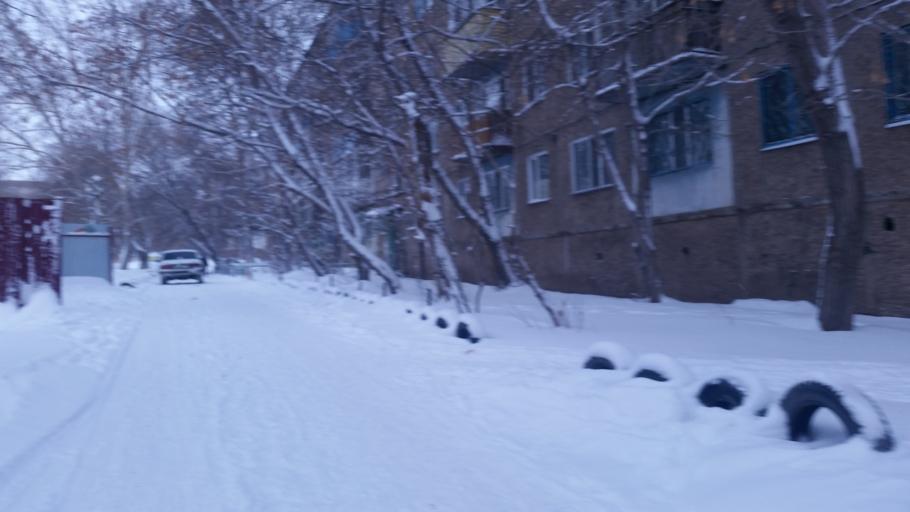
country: KZ
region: Qaraghandy
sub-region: Qaraghandy Qalasy
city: Karagandy
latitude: 49.7709
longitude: 73.1514
